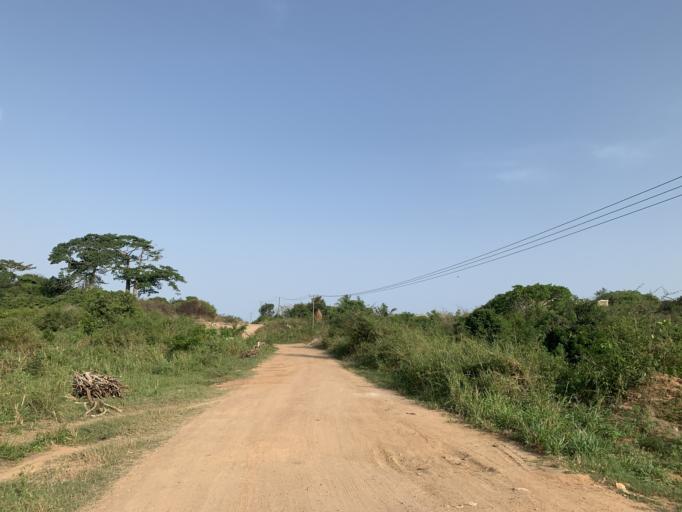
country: GH
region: Central
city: Winneba
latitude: 5.3796
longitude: -0.6176
